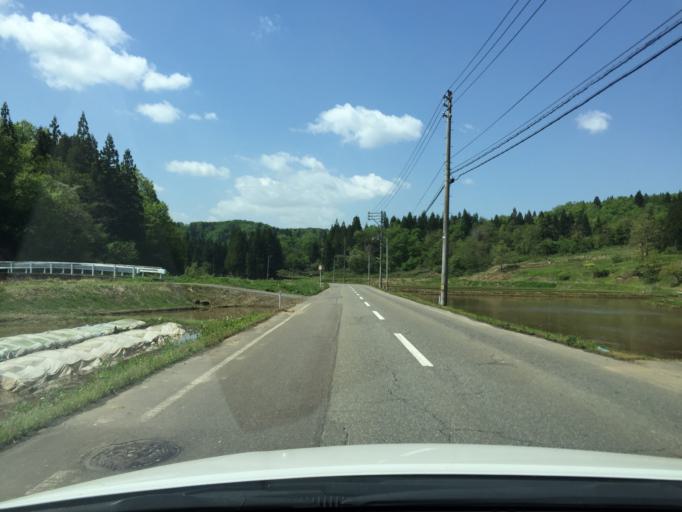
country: JP
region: Niigata
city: Tochio-honcho
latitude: 37.5077
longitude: 139.0728
